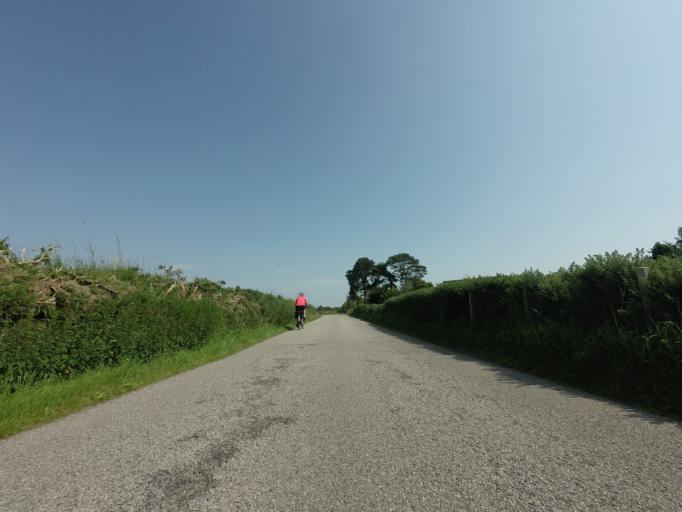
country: GB
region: Scotland
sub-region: Highland
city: Tain
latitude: 57.7984
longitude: -4.0696
